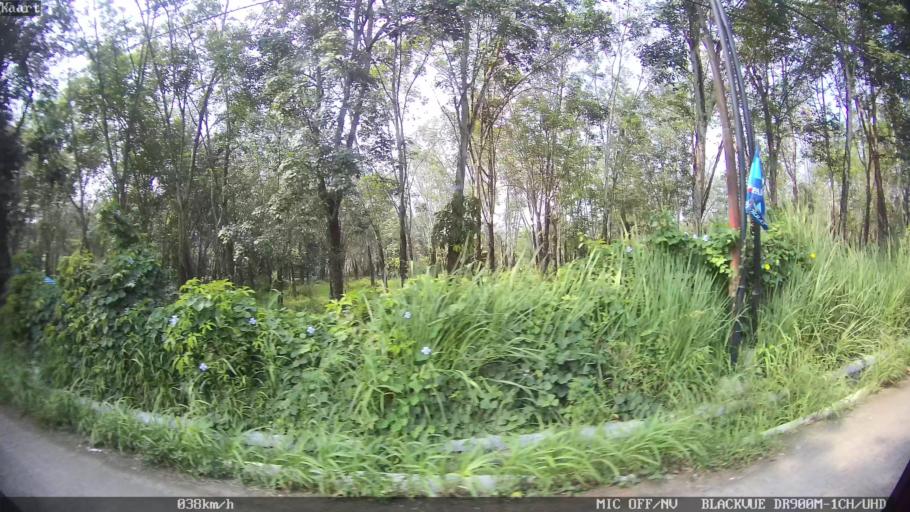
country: ID
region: Lampung
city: Gedongtataan
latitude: -5.3802
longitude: 105.1182
